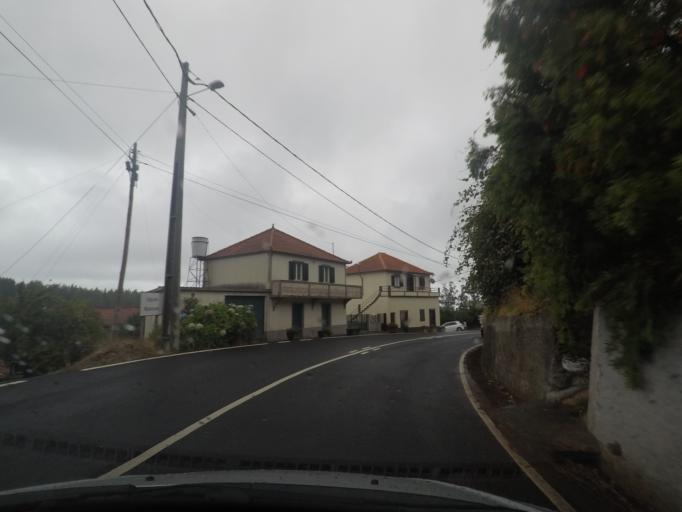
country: PT
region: Madeira
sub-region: Santa Cruz
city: Camacha
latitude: 32.6946
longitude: -16.8370
